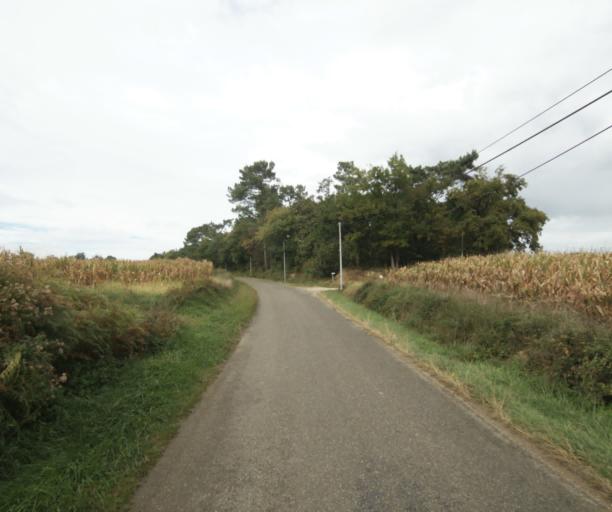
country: FR
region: Midi-Pyrenees
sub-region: Departement du Gers
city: Cazaubon
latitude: 43.8825
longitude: -0.1019
